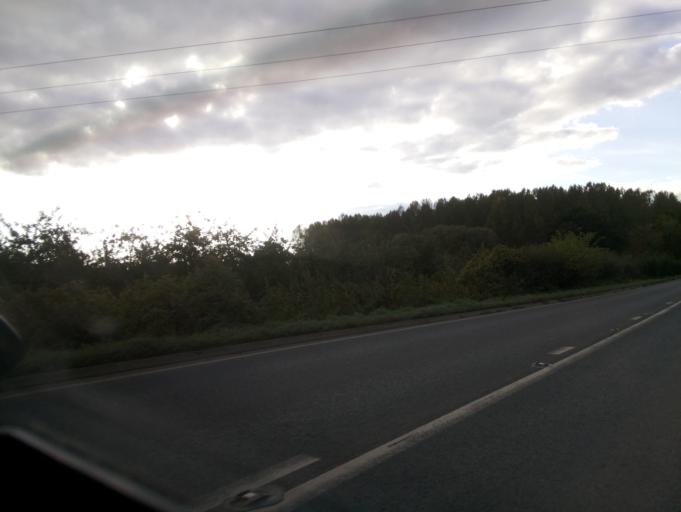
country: GB
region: England
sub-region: Herefordshire
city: Withington
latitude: 52.0597
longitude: -2.6199
